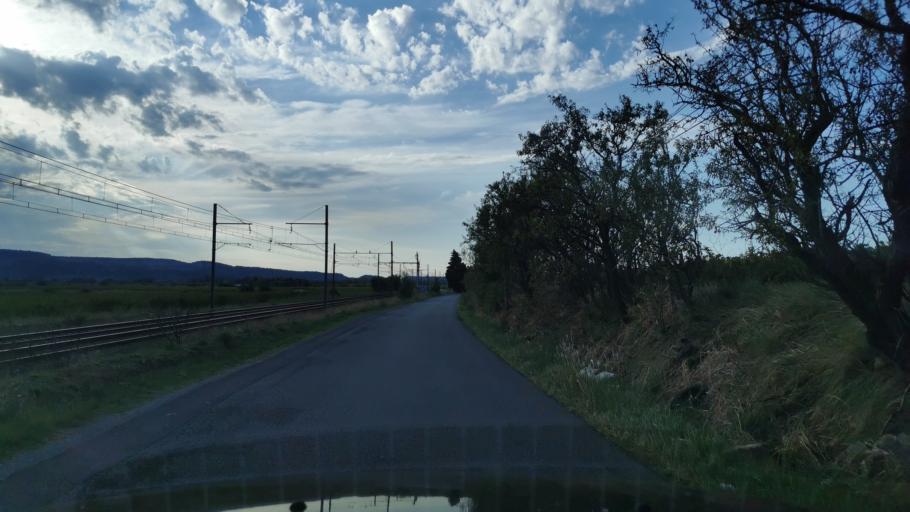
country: FR
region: Languedoc-Roussillon
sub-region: Departement de l'Aude
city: Narbonne
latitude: 43.1558
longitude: 3.0139
